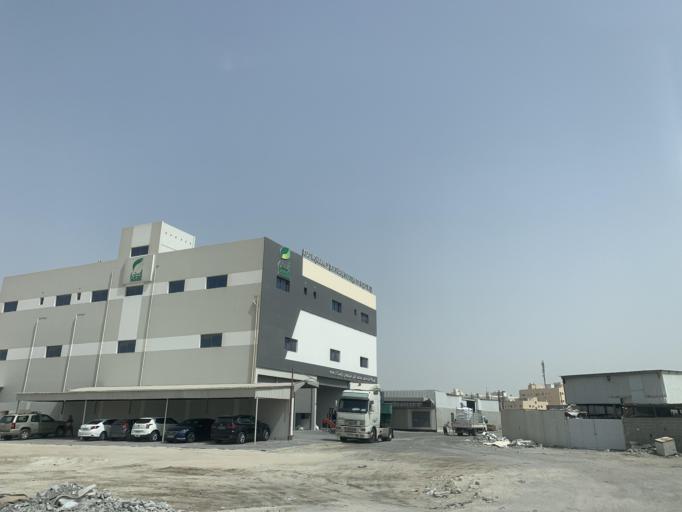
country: BH
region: Northern
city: Madinat `Isa
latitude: 26.1875
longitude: 50.5211
